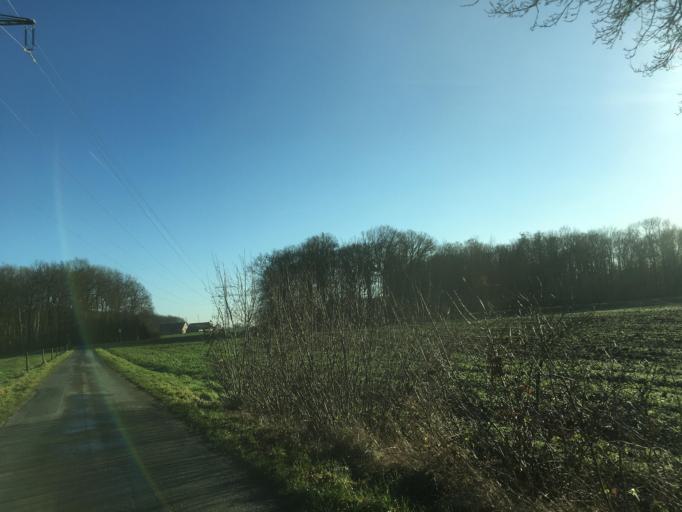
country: DE
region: North Rhine-Westphalia
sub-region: Regierungsbezirk Munster
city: Dulmen
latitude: 51.8512
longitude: 7.3082
